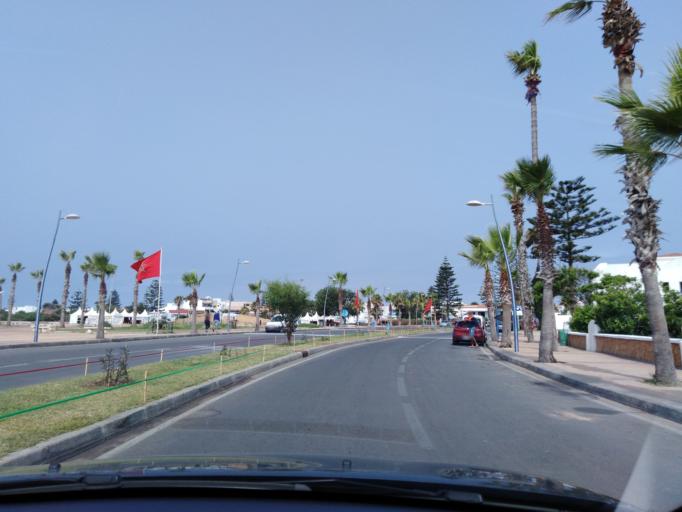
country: MA
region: Doukkala-Abda
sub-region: Safi
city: Safi
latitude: 32.7327
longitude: -9.0420
